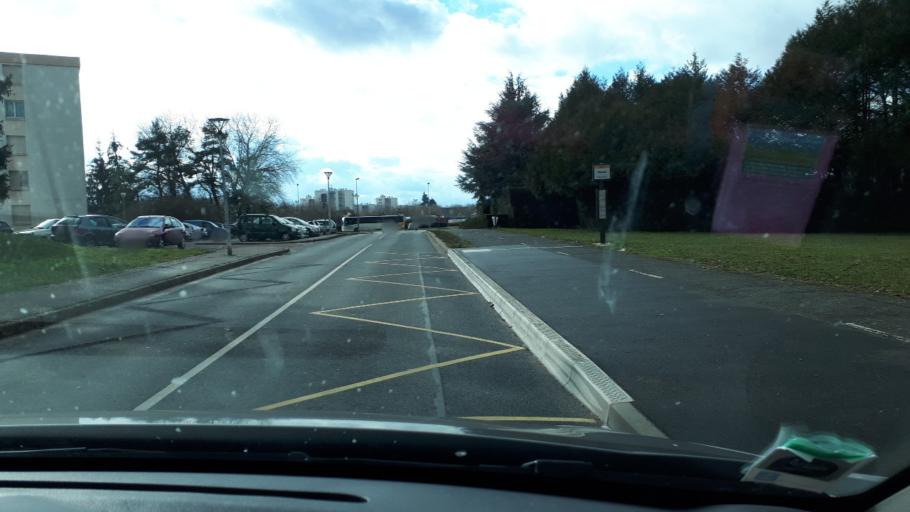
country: FR
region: Centre
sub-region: Departement du Loir-et-Cher
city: Villebarou
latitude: 47.5980
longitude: 1.3071
